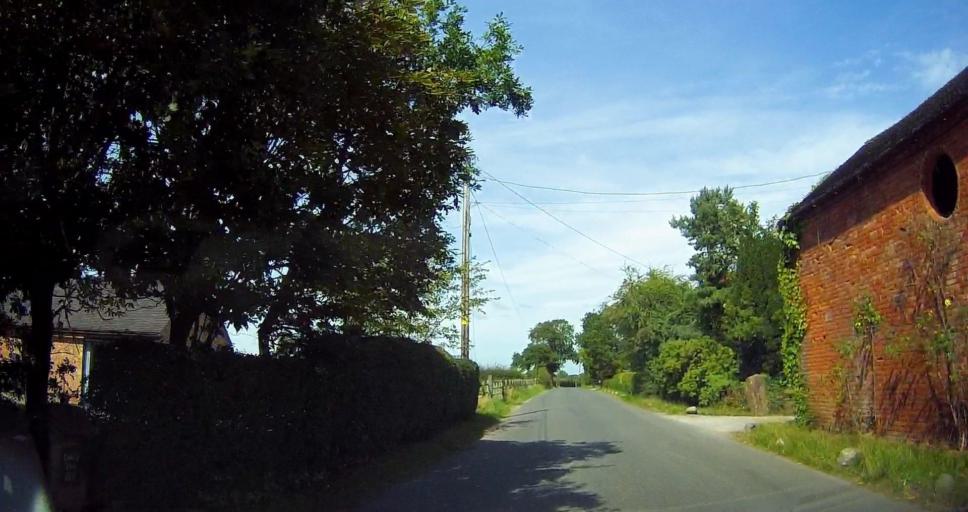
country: GB
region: England
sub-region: Cheshire East
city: Nantwich
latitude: 52.9962
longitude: -2.5340
